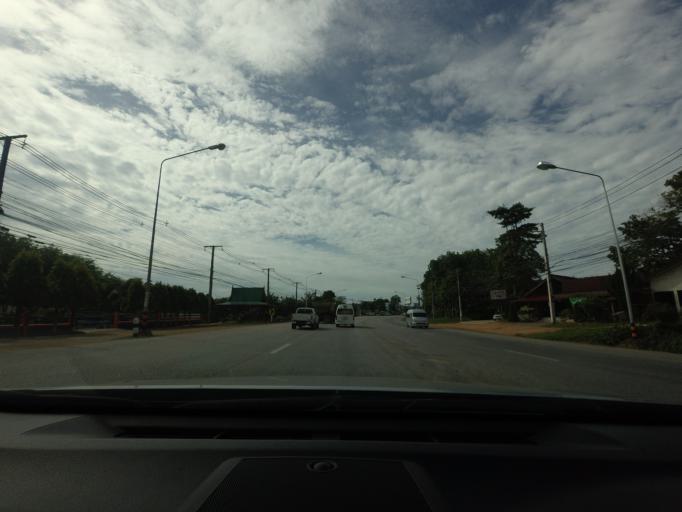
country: TH
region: Songkhla
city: Hat Yai
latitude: 6.9801
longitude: 100.4263
